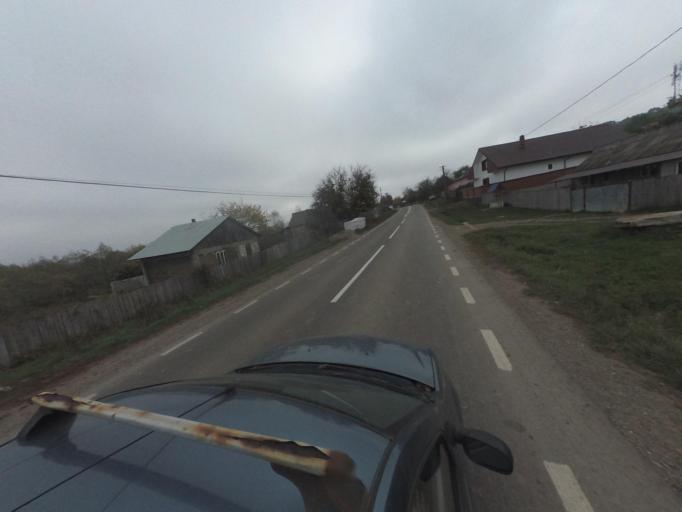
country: RO
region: Vaslui
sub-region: Comuna Bacesti
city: Bacesti
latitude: 46.8363
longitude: 27.2288
